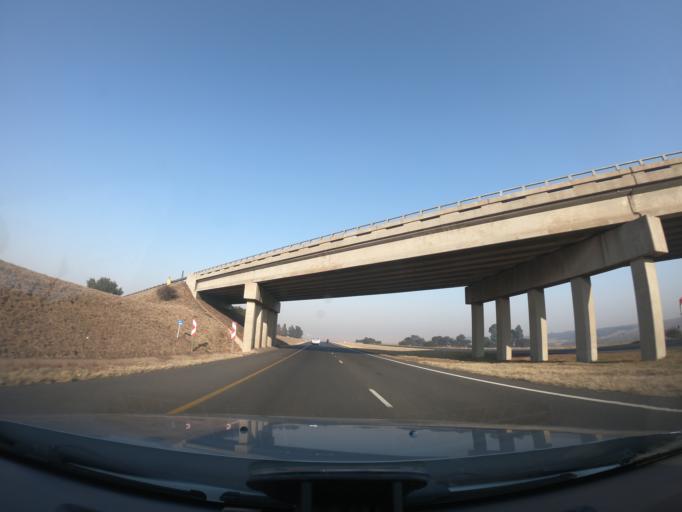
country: ZA
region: Mpumalanga
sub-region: Nkangala District Municipality
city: Middelburg
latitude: -25.8444
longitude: 29.4031
